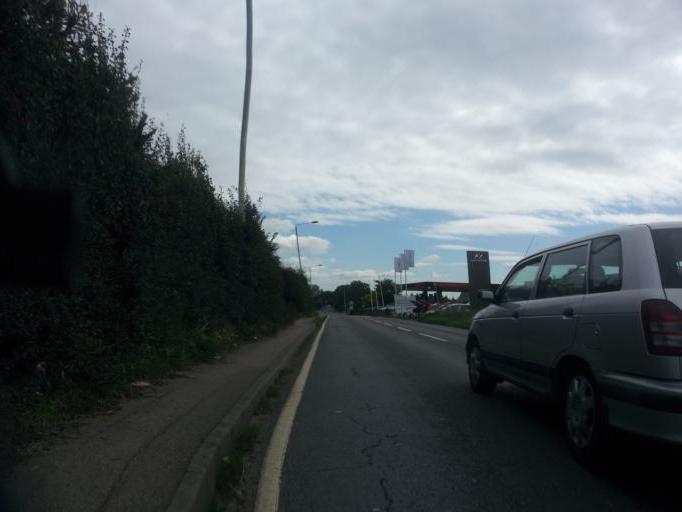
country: GB
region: England
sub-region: Kent
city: Rainham
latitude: 51.3591
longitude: 0.6301
